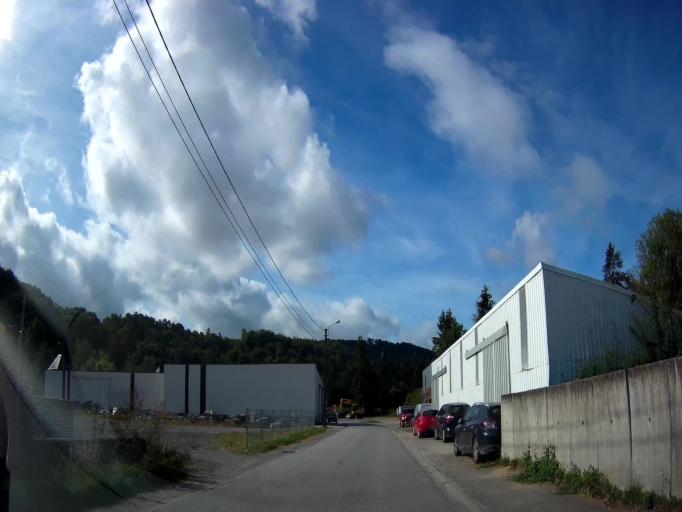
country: BE
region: Wallonia
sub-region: Province de Namur
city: Rochefort
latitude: 50.1574
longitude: 5.2172
